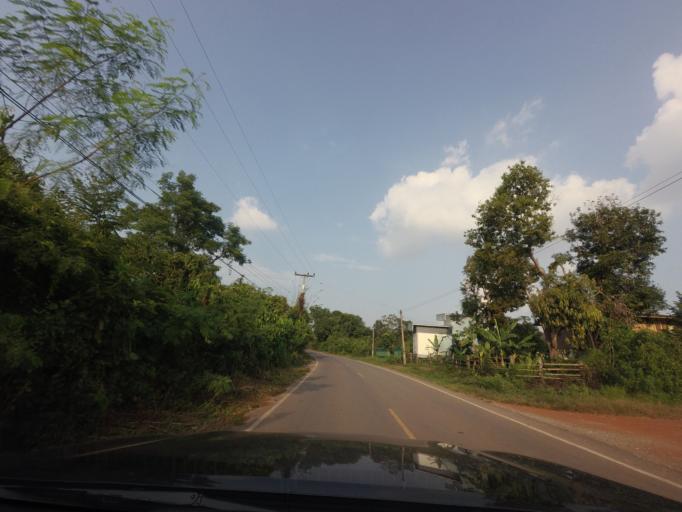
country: TH
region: Nan
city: Nan
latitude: 18.7728
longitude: 100.7341
